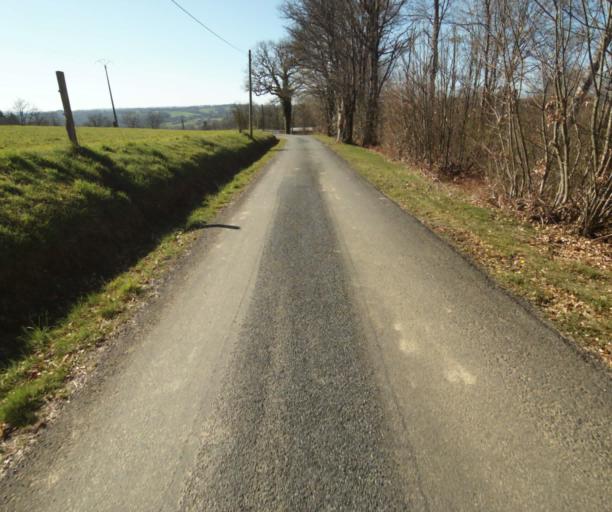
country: FR
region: Limousin
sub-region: Departement de la Correze
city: Chamboulive
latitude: 45.4374
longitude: 1.6690
